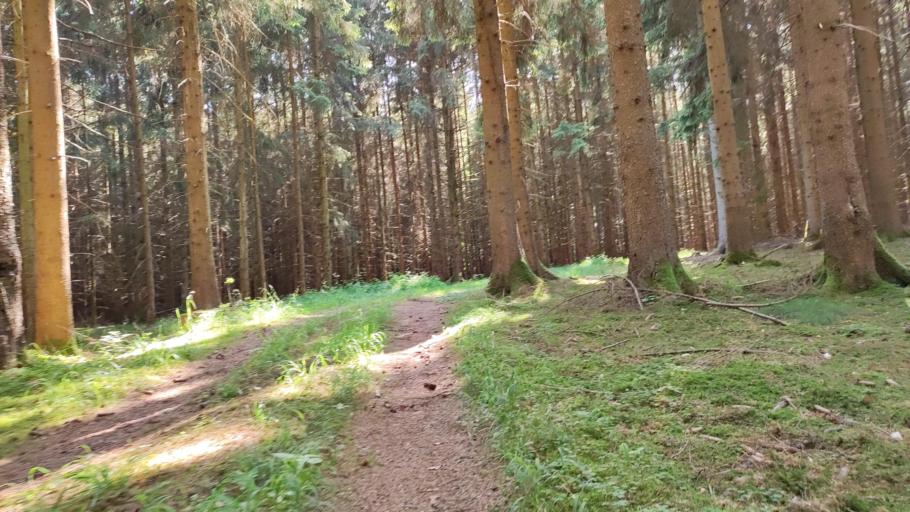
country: DE
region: Bavaria
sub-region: Swabia
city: Dinkelscherben
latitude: 48.3692
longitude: 10.6002
